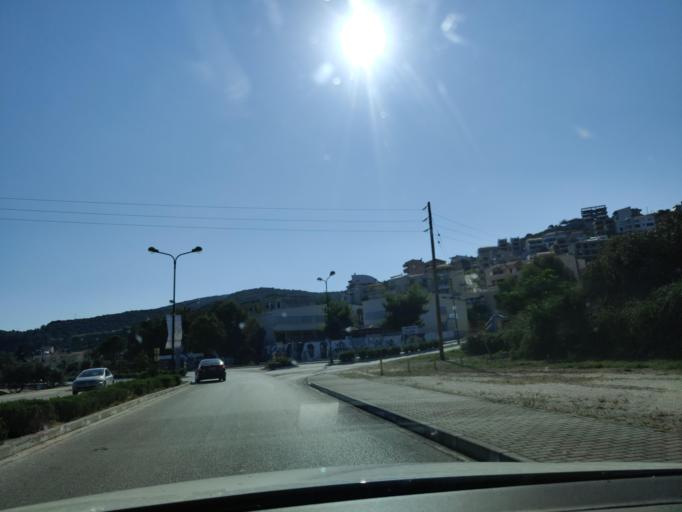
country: GR
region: East Macedonia and Thrace
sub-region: Nomos Kavalas
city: Nea Peramos
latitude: 40.8492
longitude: 24.3105
